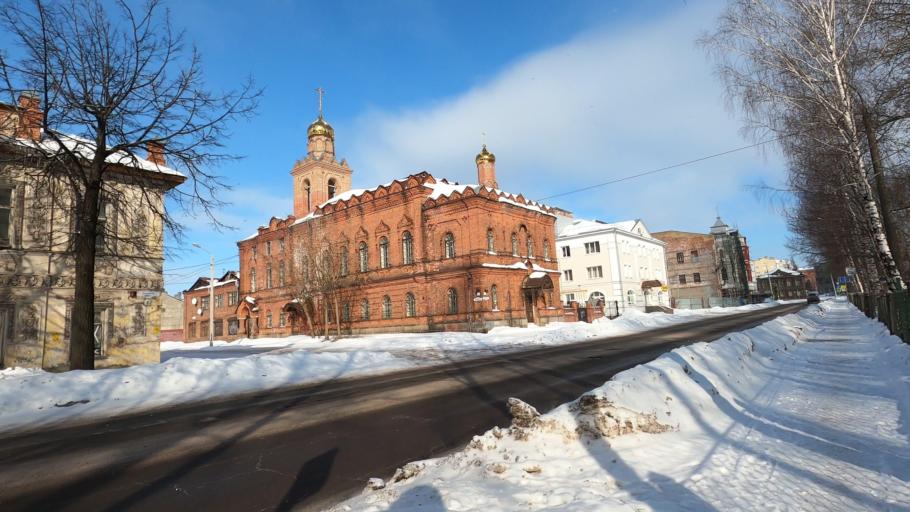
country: RU
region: Jaroslavl
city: Rybinsk
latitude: 58.0447
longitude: 38.8502
